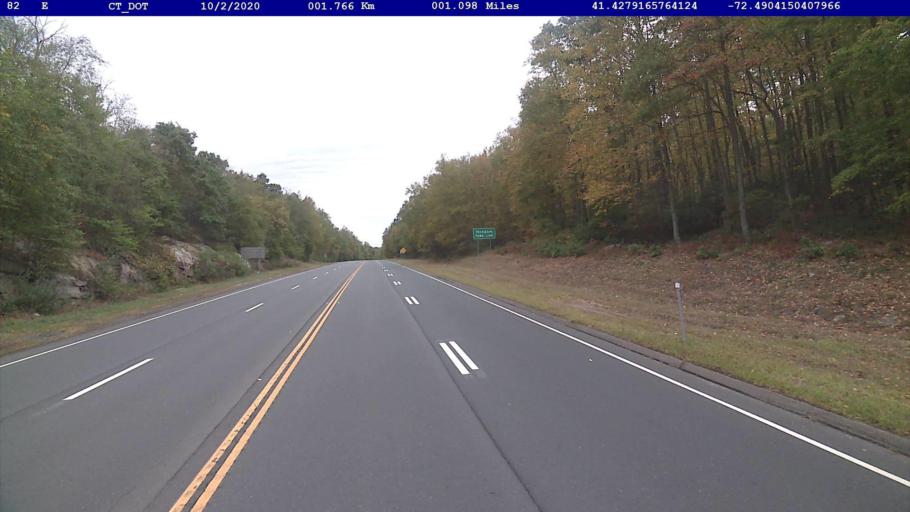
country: US
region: Connecticut
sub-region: Middlesex County
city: East Haddam
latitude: 41.4279
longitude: -72.4904
